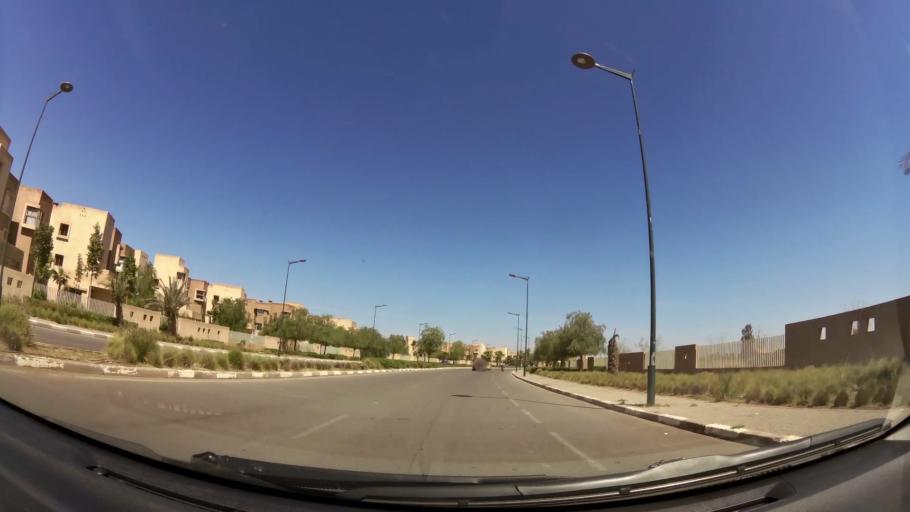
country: MA
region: Marrakech-Tensift-Al Haouz
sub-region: Marrakech
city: Marrakesh
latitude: 31.5965
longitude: -8.0054
